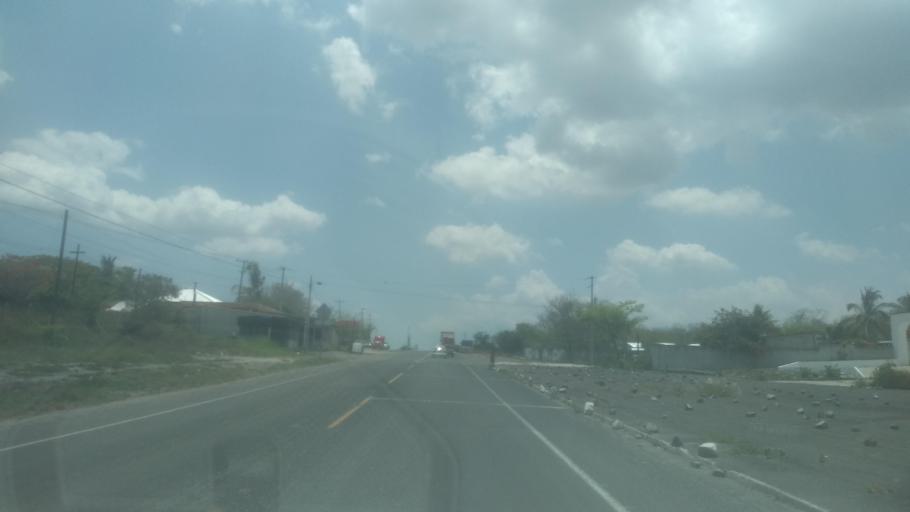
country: MX
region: Veracruz
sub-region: Emiliano Zapata
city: Plan del Rio
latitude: 19.3923
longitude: -96.6309
